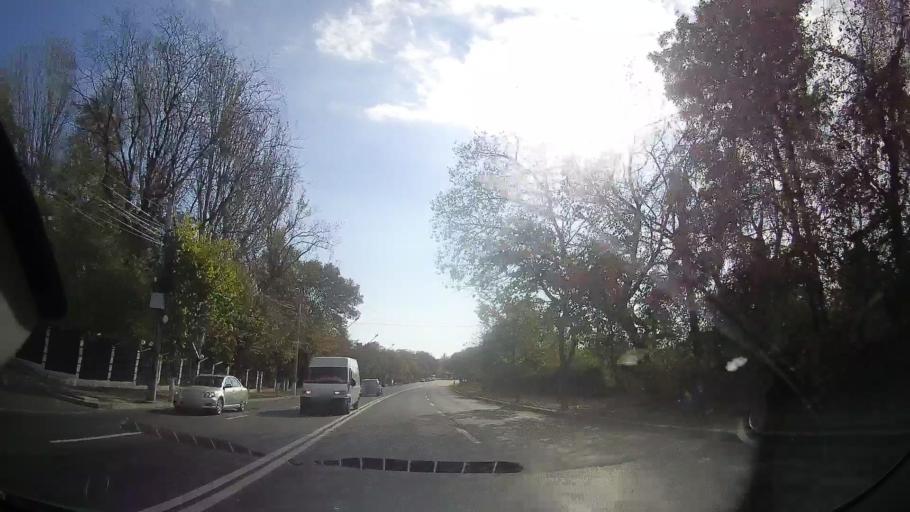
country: RO
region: Constanta
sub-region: Oras Eforie
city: Eforie
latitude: 44.0325
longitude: 28.6469
